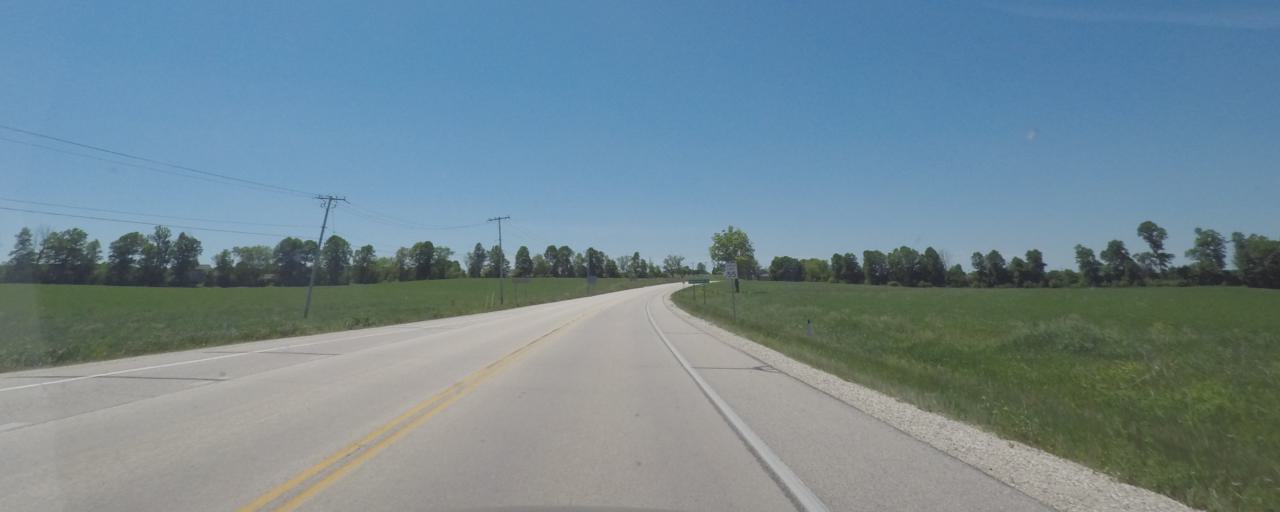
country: US
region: Wisconsin
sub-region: Ozaukee County
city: Kohler
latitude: 43.5117
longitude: -88.1165
